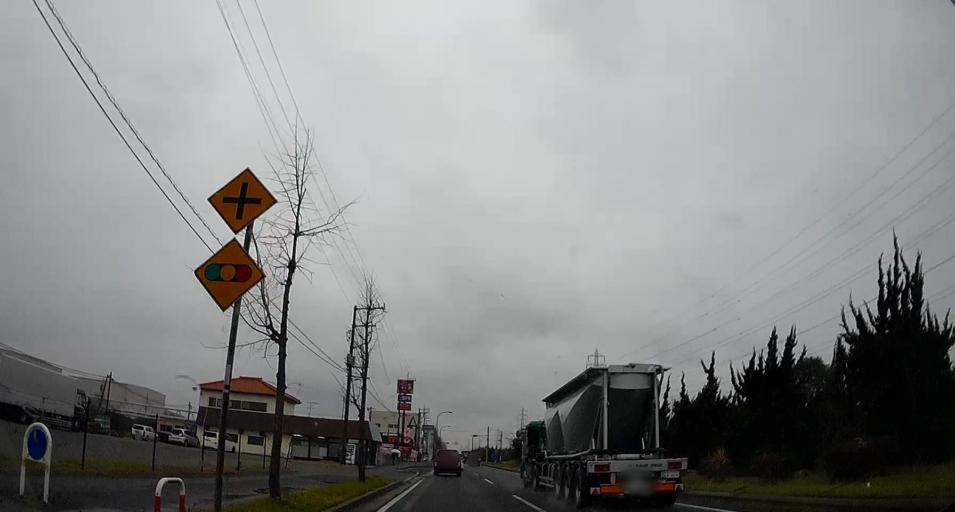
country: JP
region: Chiba
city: Ichihara
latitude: 35.5012
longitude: 140.0498
